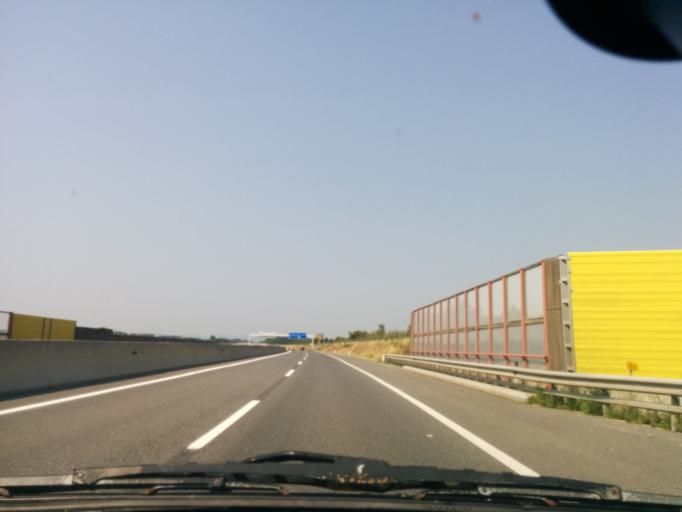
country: AT
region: Lower Austria
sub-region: Politischer Bezirk Tulln
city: Grafenworth
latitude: 48.4117
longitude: 15.7660
